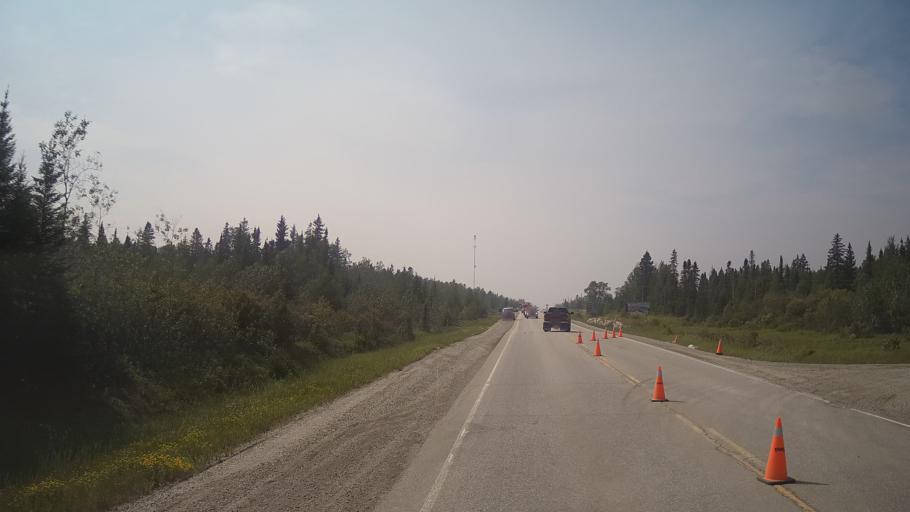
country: CA
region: Ontario
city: Kapuskasing
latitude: 49.3163
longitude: -82.0510
